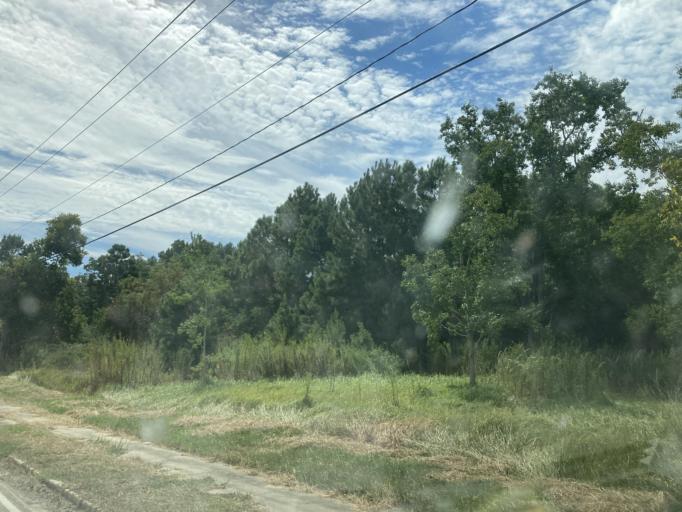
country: US
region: Mississippi
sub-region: Harrison County
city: D'Iberville
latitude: 30.4334
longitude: -88.8810
